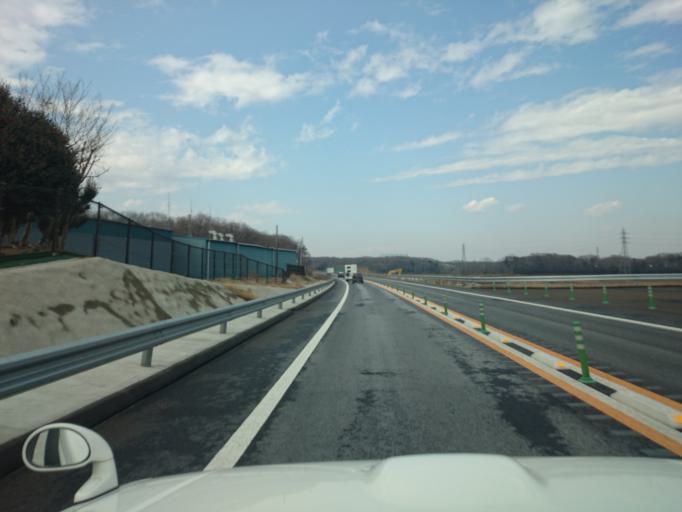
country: JP
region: Ibaraki
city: Iwai
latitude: 36.0811
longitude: 139.9145
